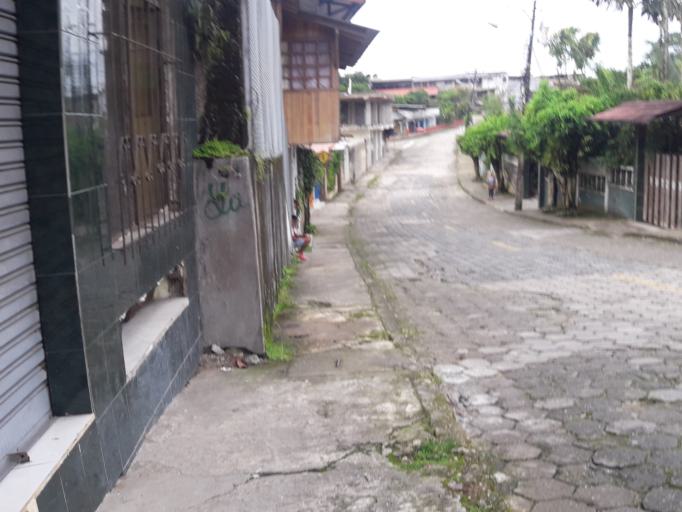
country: EC
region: Napo
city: Tena
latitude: -0.9941
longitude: -77.8143
